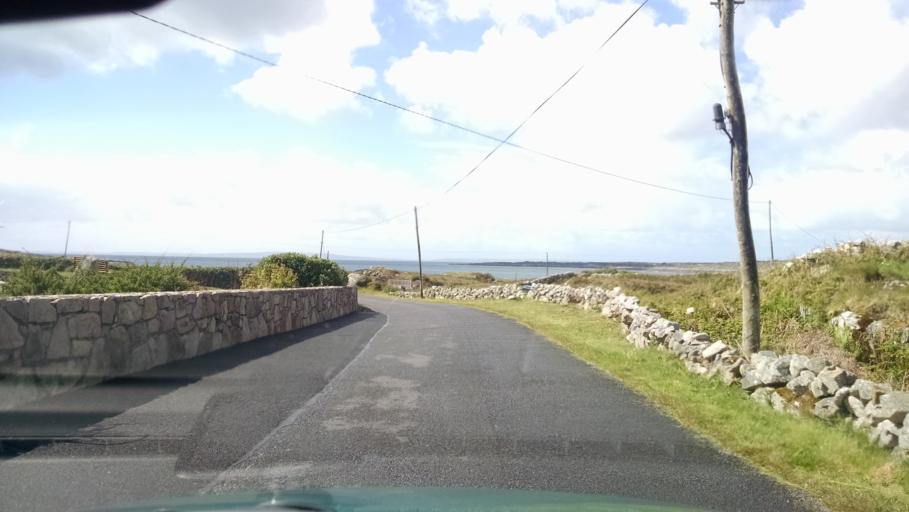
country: IE
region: Connaught
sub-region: County Galway
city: Oughterard
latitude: 53.2469
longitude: -9.6247
